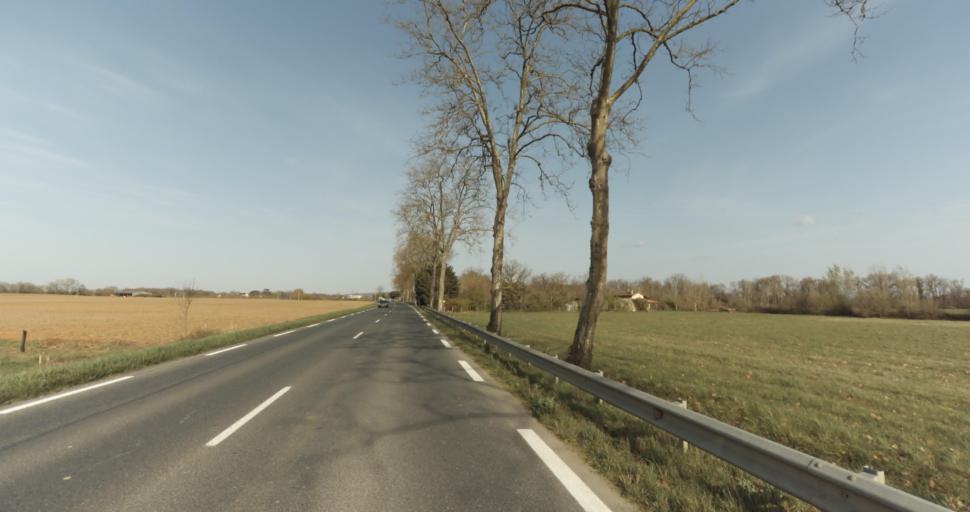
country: FR
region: Midi-Pyrenees
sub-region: Departement du Tarn
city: Saint-Sulpice-la-Pointe
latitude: 43.7560
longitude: 1.7169
